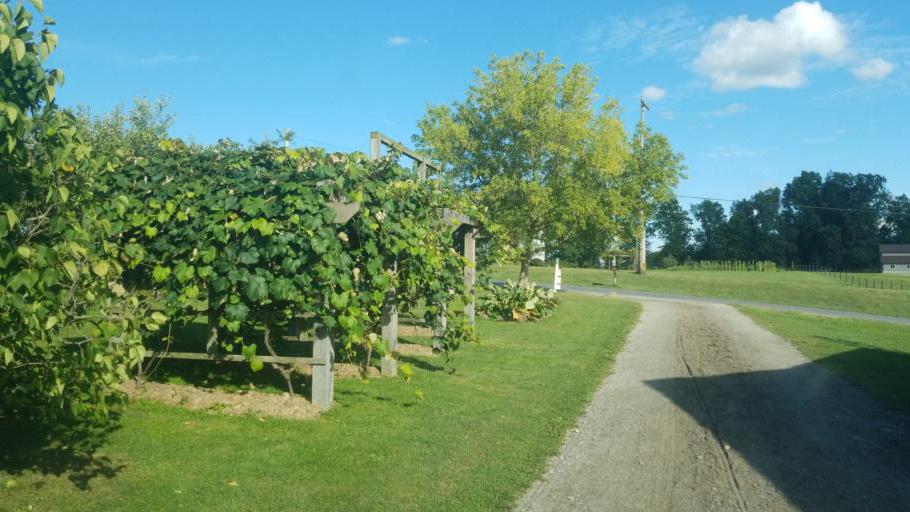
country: US
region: Ohio
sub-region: Geauga County
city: Middlefield
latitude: 41.4569
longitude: -80.9836
